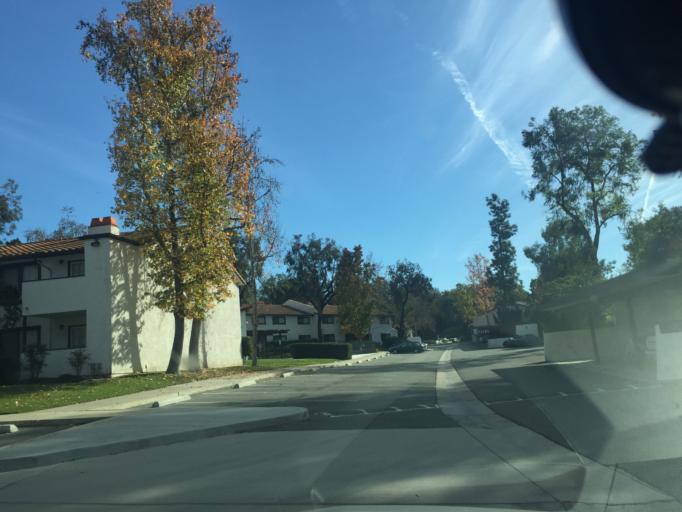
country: US
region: California
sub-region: San Diego County
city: Lemon Grove
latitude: 32.7690
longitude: -117.0872
